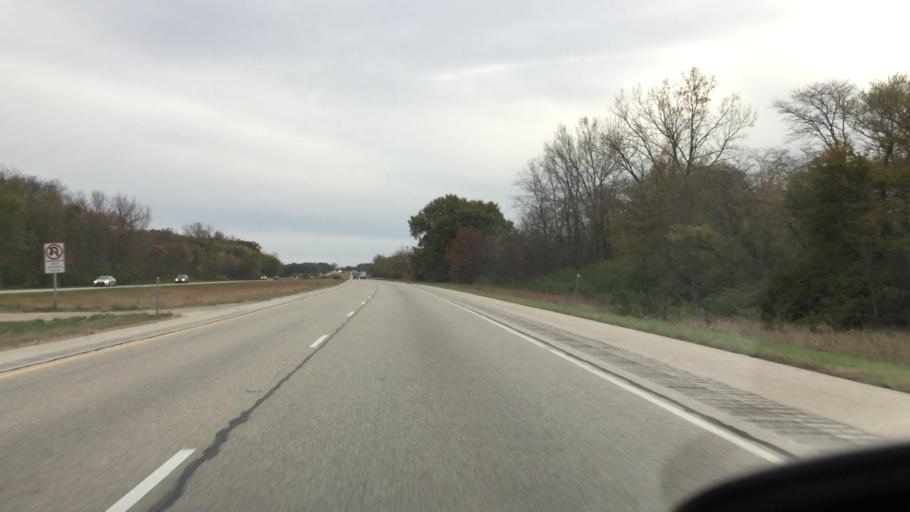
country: US
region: Illinois
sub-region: McLean County
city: Twin Grove
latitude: 40.3773
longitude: -89.0950
